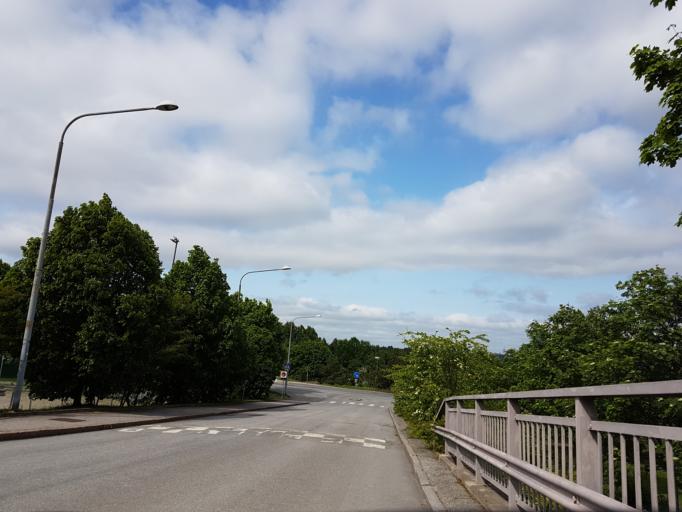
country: SE
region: Stockholm
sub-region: Sundbybergs Kommun
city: Sundbyberg
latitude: 59.3765
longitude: 17.9654
